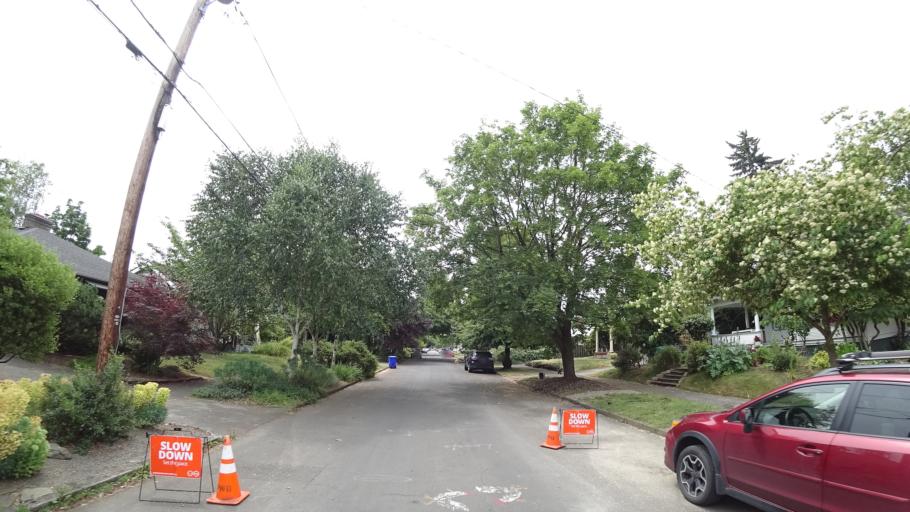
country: US
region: Oregon
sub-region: Multnomah County
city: Portland
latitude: 45.5676
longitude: -122.6936
